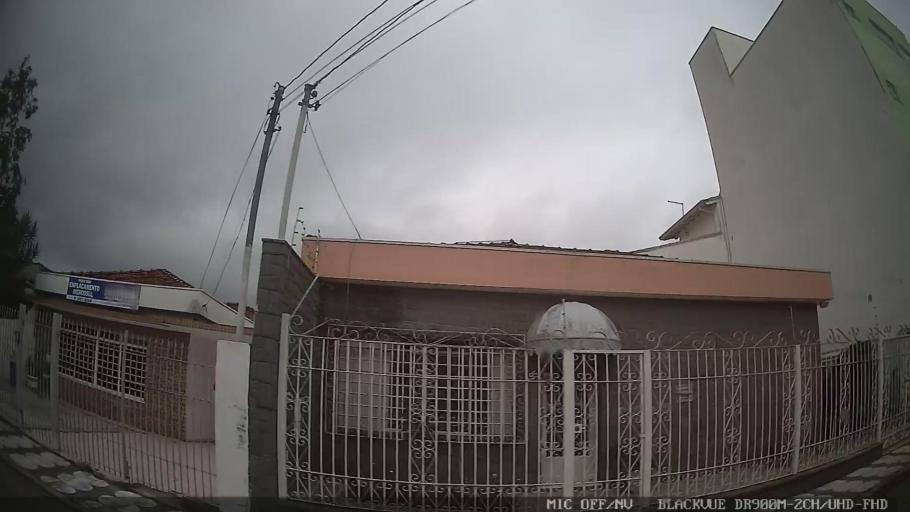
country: BR
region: Sao Paulo
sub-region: Mogi das Cruzes
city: Mogi das Cruzes
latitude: -23.5168
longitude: -46.1942
